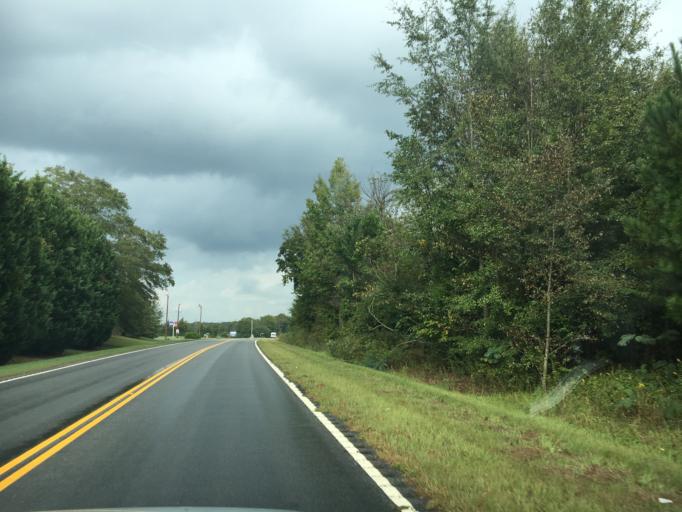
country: US
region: Georgia
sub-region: Hart County
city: Reed Creek
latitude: 34.3964
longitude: -82.8065
